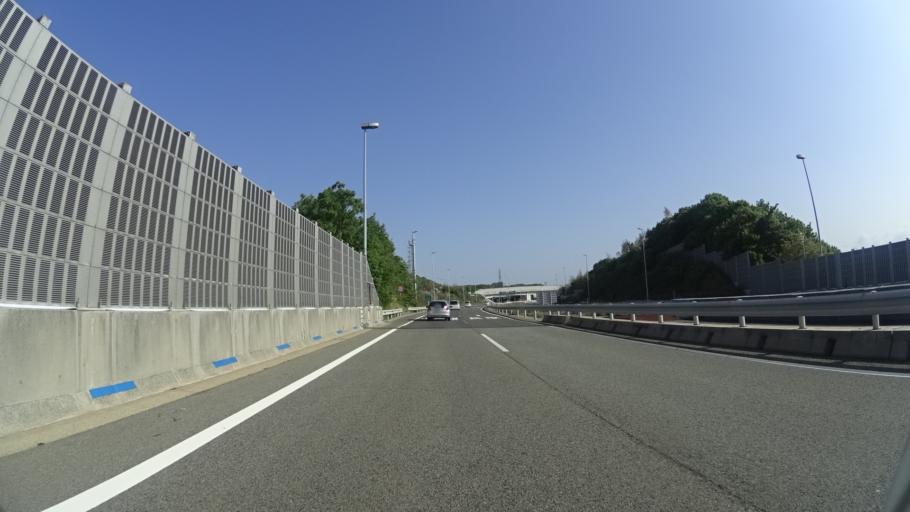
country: JP
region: Hyogo
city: Akashi
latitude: 34.6533
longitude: 135.0680
